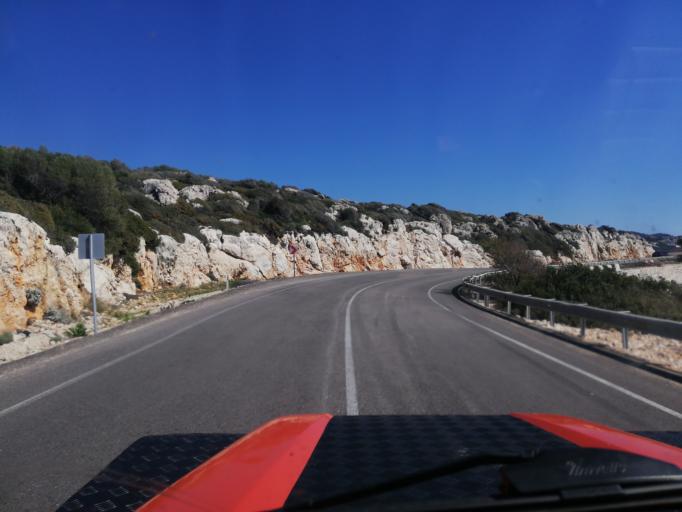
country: GR
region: South Aegean
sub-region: Nomos Dodekanisou
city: Megisti
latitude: 36.2031
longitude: 29.5785
